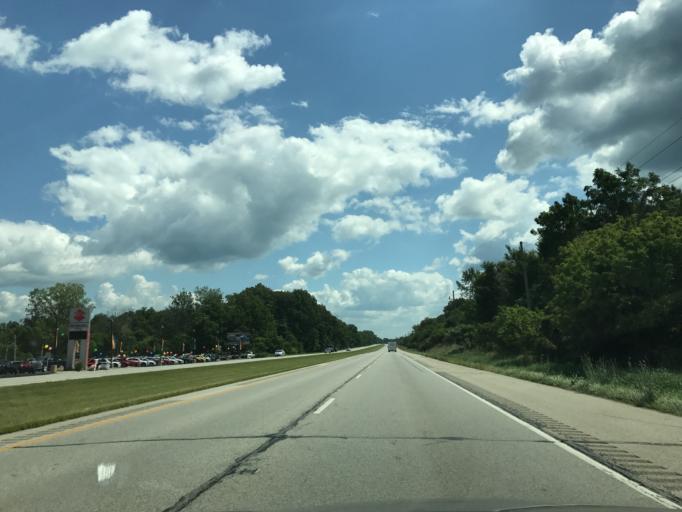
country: US
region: Indiana
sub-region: Kosciusko County
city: Winona Lake
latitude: 41.2177
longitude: -85.7679
